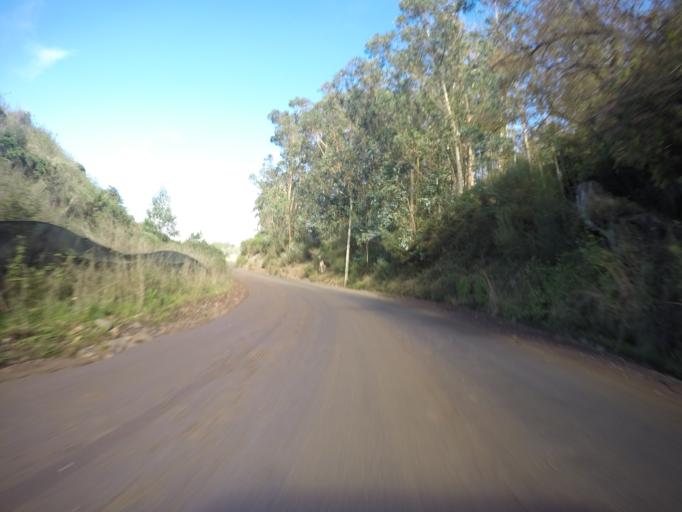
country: PT
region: Madeira
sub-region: Santa Cruz
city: Camacha
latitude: 32.6917
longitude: -16.8762
